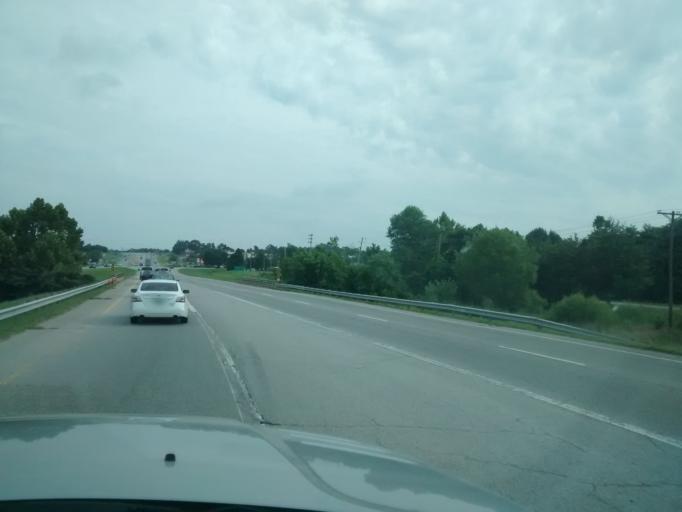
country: US
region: Arkansas
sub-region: Washington County
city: Johnson
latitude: 36.1187
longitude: -94.1449
